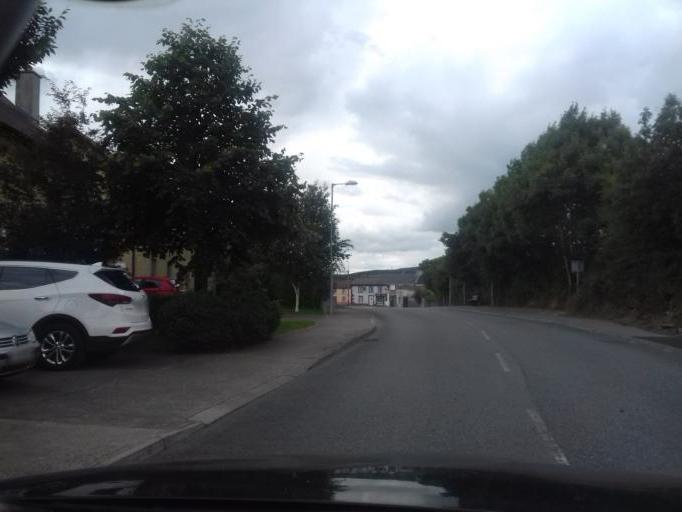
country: IE
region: Leinster
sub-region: County Carlow
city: Bagenalstown
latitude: 52.6805
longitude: -7.0272
